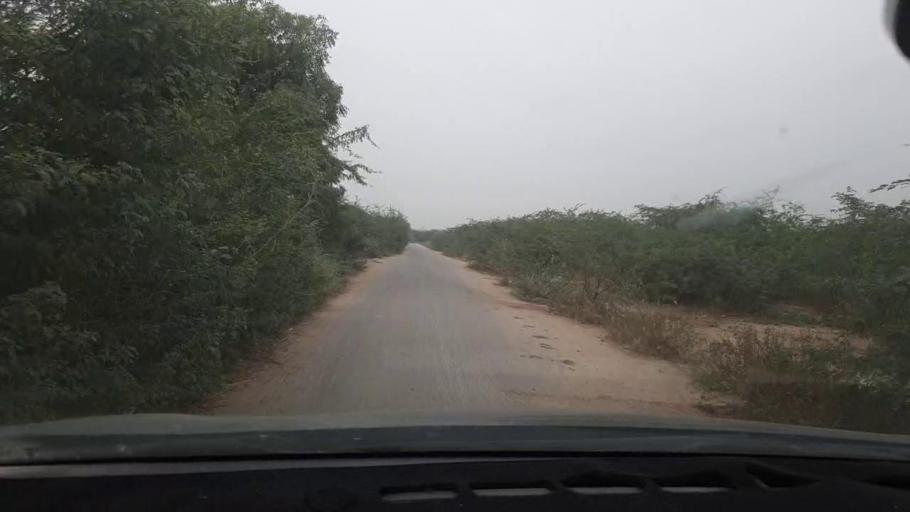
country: PK
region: Sindh
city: Malir Cantonment
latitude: 24.9257
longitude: 67.3231
